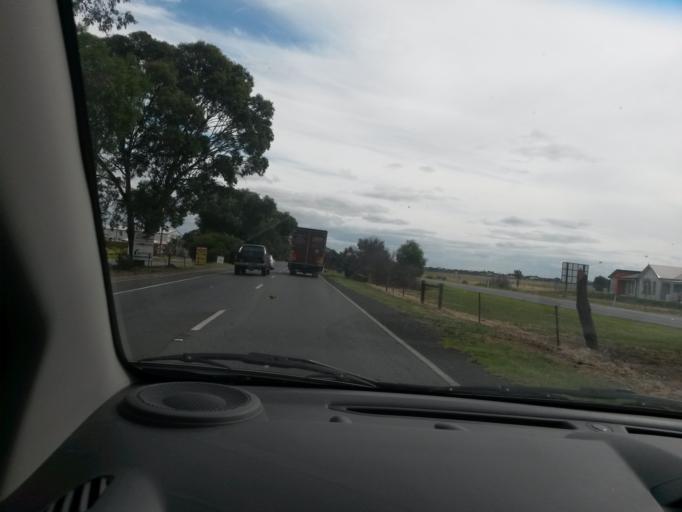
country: AU
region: South Australia
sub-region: Salisbury
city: Salisbury
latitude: -34.7967
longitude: 138.6426
